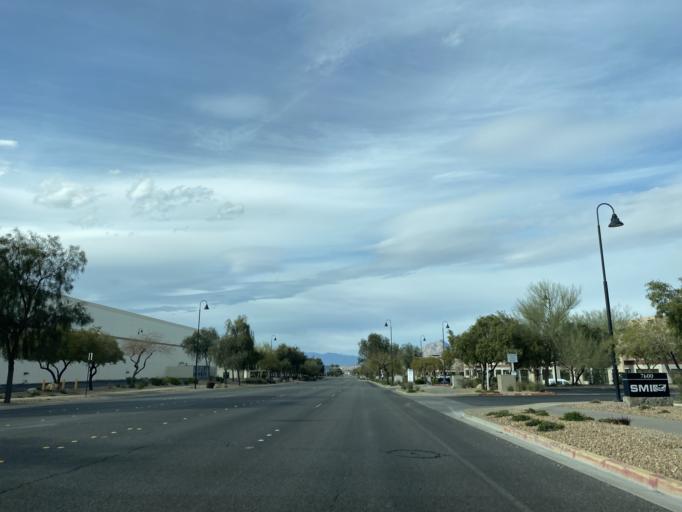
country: US
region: Nevada
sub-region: Clark County
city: Henderson
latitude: 36.0514
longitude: -115.0198
